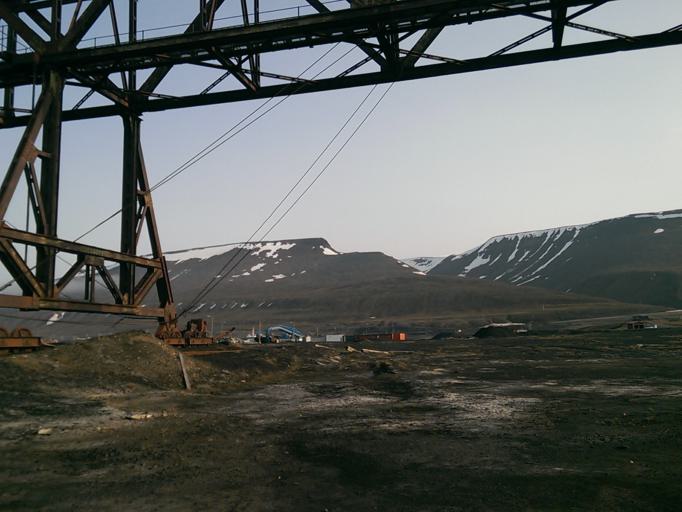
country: SJ
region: Svalbard
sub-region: Spitsbergen
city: Longyearbyen
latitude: 78.2472
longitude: 15.5412
